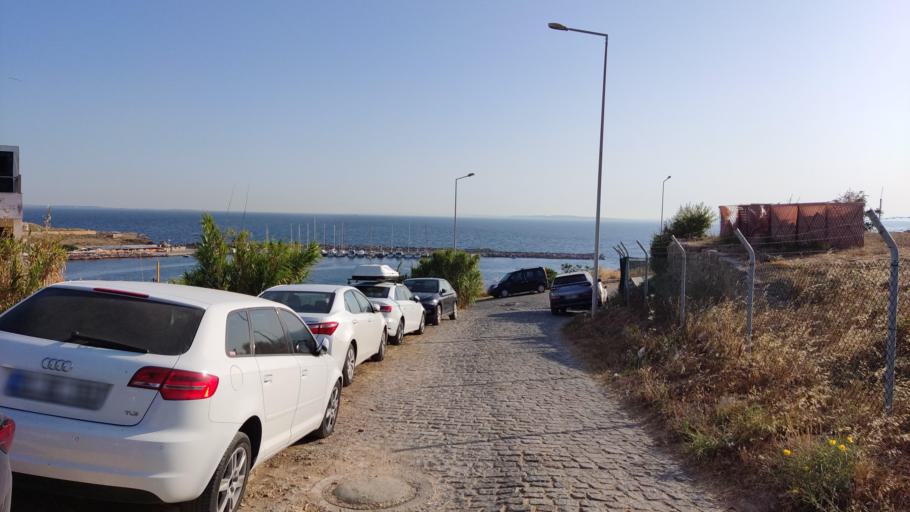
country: TR
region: Canakkale
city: Bozcaada
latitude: 39.8328
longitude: 26.0738
